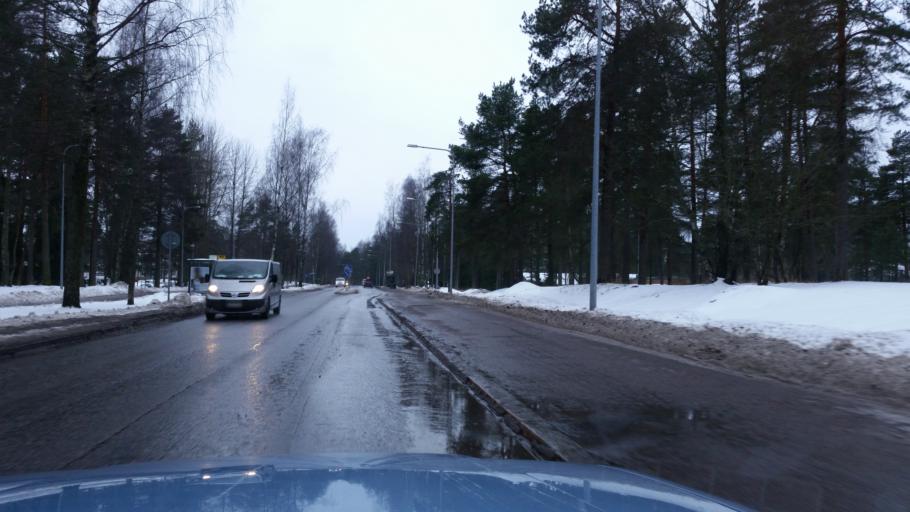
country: FI
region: Uusimaa
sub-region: Helsinki
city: Vantaa
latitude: 60.2276
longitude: 25.0647
